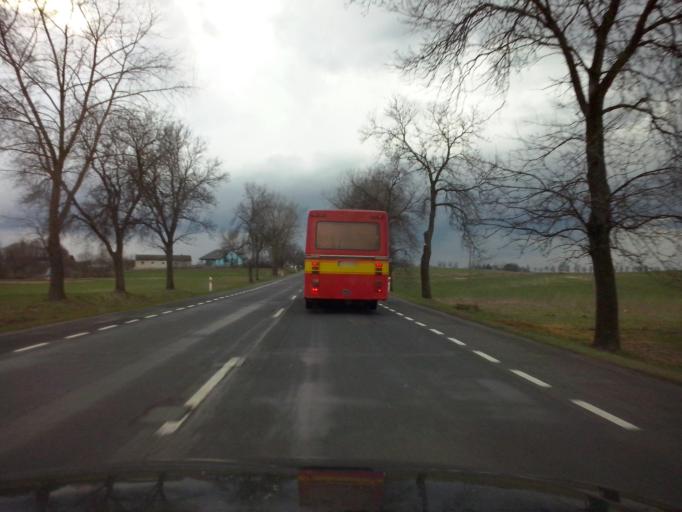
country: PL
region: Lublin Voivodeship
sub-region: Powiat chelmski
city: Rejowiec Fabryczny
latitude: 51.1732
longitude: 23.2799
